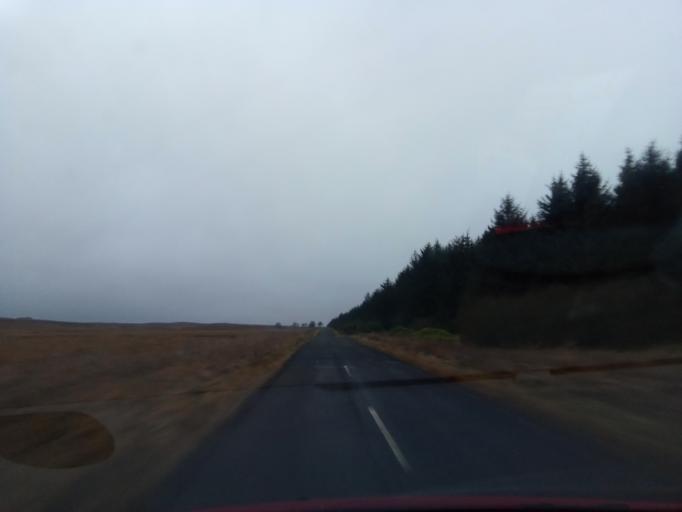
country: GB
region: England
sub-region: Northumberland
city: Rothley
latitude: 55.2058
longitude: -2.0215
